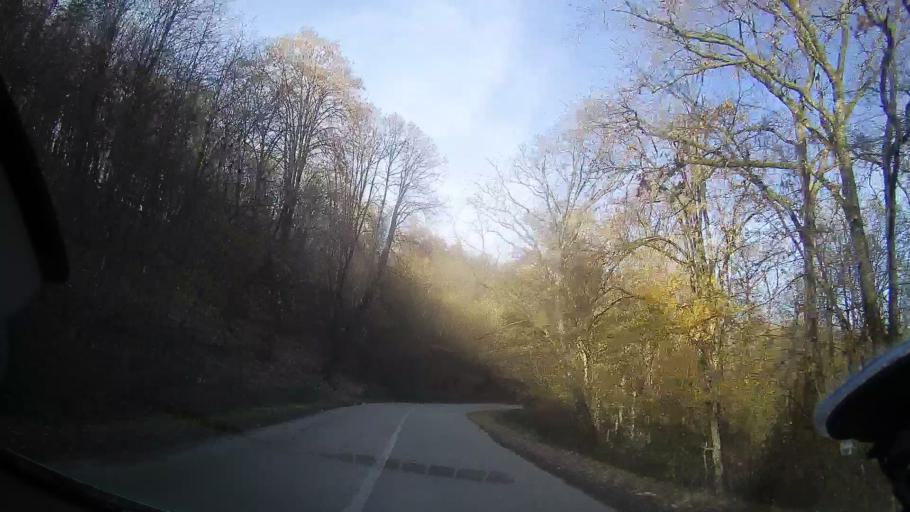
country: RO
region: Bihor
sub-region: Comuna Brusturi
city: Brusturi
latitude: 47.1038
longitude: 22.2468
